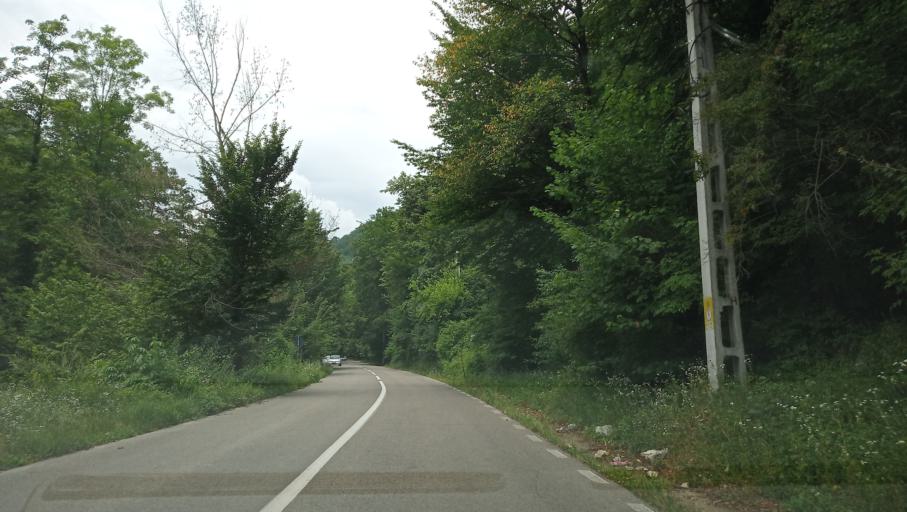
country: RO
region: Gorj
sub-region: Comuna Tismana
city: Pocruia
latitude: 45.0761
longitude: 22.9307
